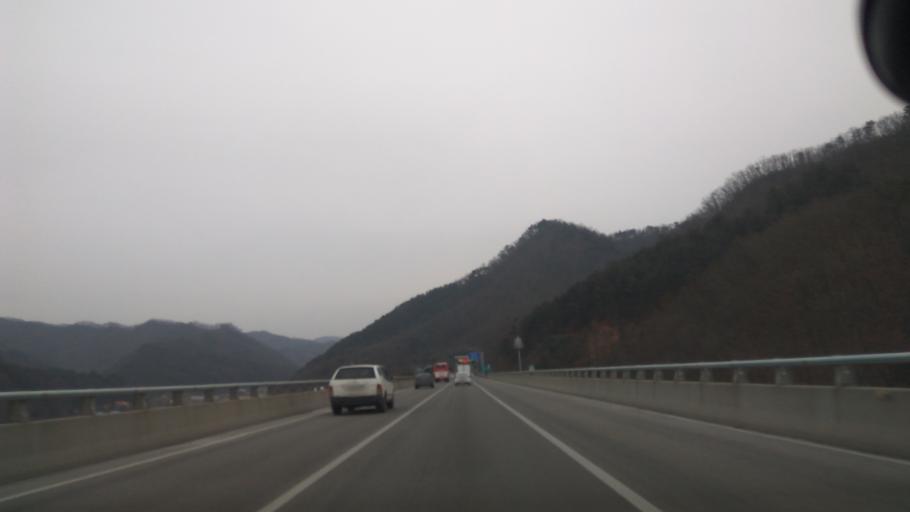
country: KR
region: Gyeonggi-do
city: Gapyeong
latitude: 37.7253
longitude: 127.5894
